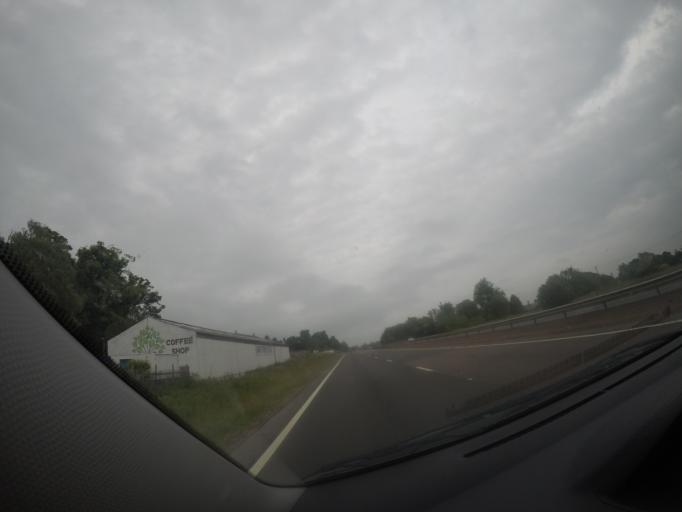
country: GB
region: Scotland
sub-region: Perth and Kinross
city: Abernethy
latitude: 56.3786
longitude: -3.3038
